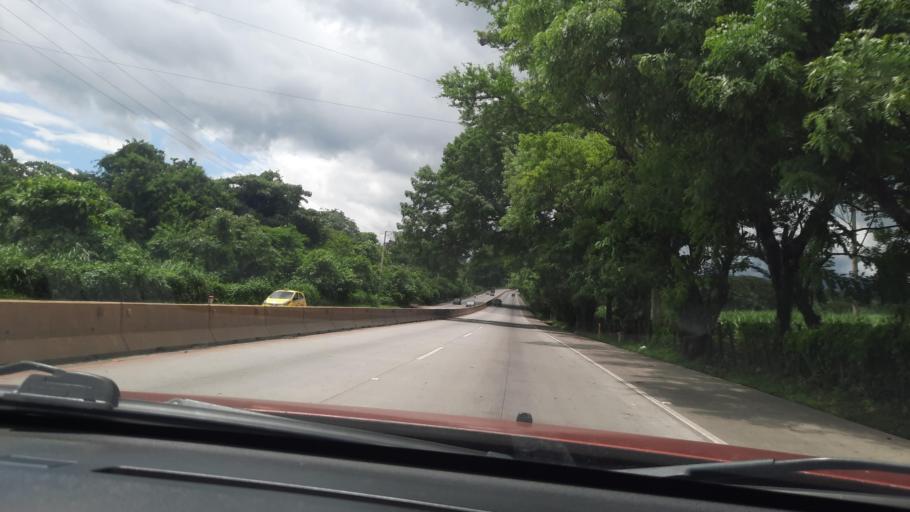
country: SV
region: Sonsonate
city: Sonzacate
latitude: 13.7300
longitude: -89.7015
